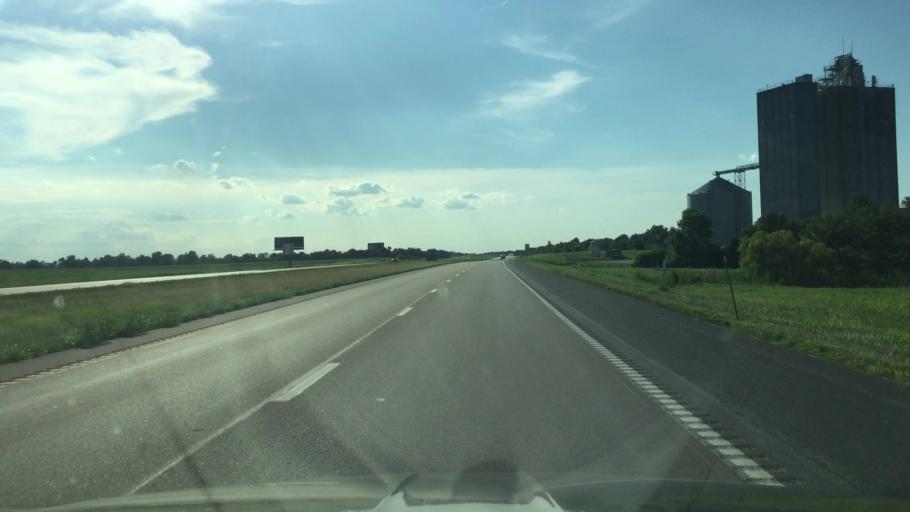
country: US
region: Missouri
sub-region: Pettis County
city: La Monte
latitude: 38.7489
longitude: -93.3436
